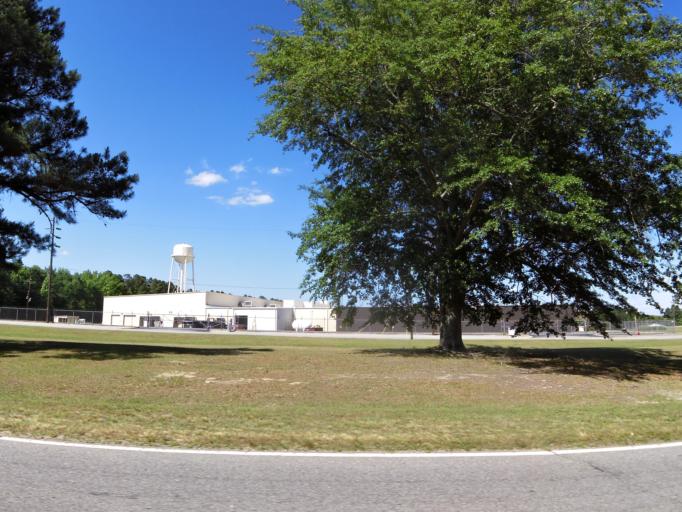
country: US
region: South Carolina
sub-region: Barnwell County
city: Williston
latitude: 33.3919
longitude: -81.4027
